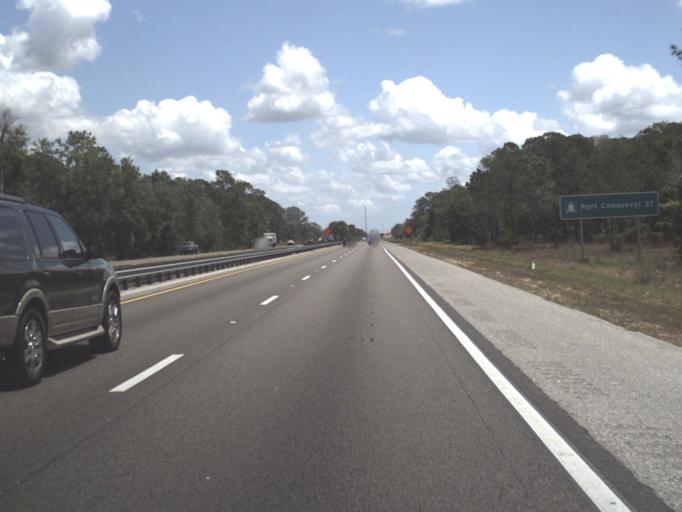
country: US
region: Florida
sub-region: Orange County
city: Alafaya
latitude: 28.4515
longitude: -81.1894
